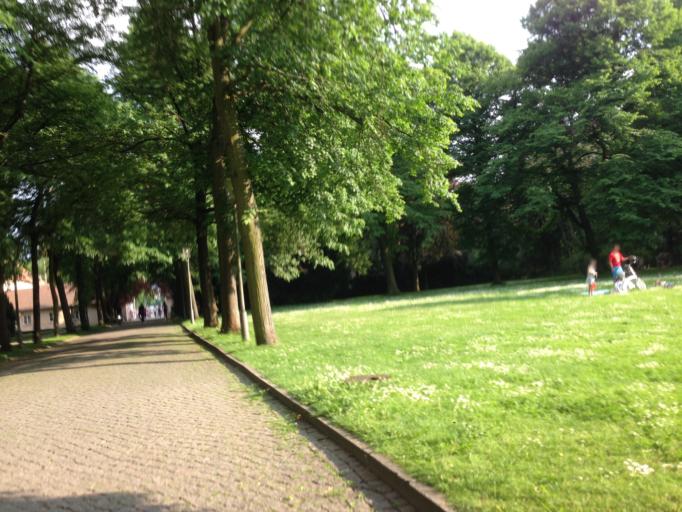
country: DE
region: Berlin
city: Niederschonhausen
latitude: 52.5779
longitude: 13.4054
